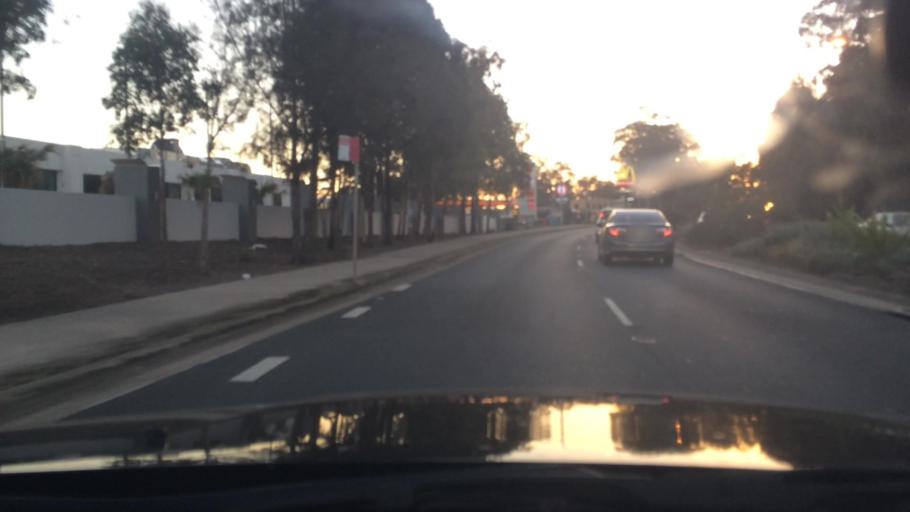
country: AU
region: New South Wales
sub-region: Fairfield
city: Fairfield Heights
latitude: -33.8506
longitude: 150.8999
